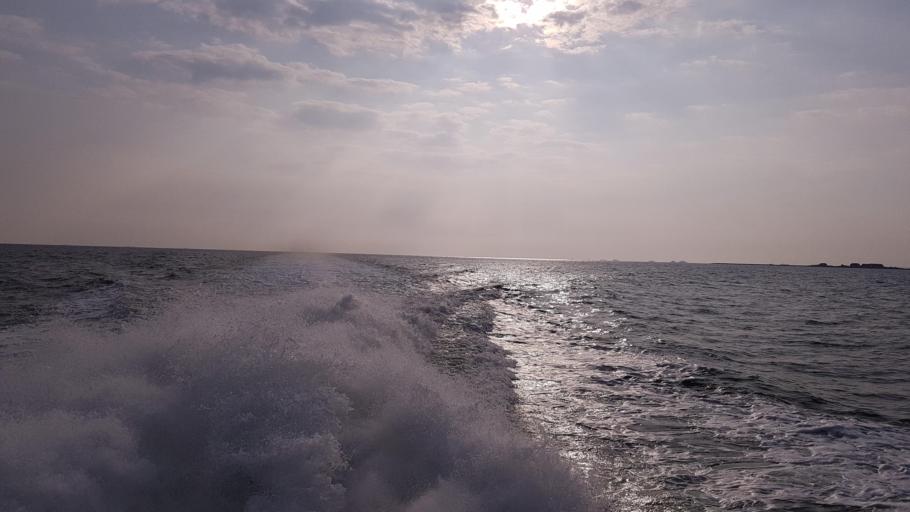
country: DE
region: Schleswig-Holstein
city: Grode
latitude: 54.6218
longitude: 8.7492
